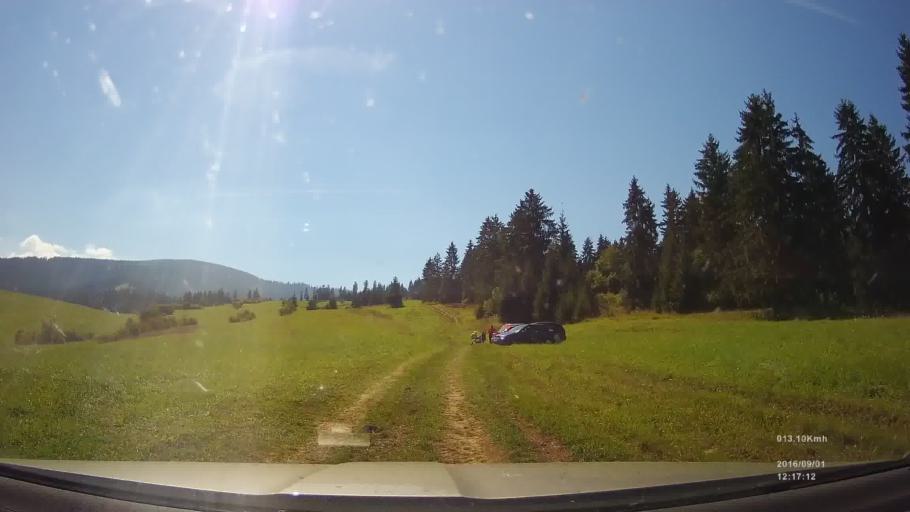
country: SK
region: Zilinsky
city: Ruzomberok
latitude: 49.0419
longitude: 19.4296
